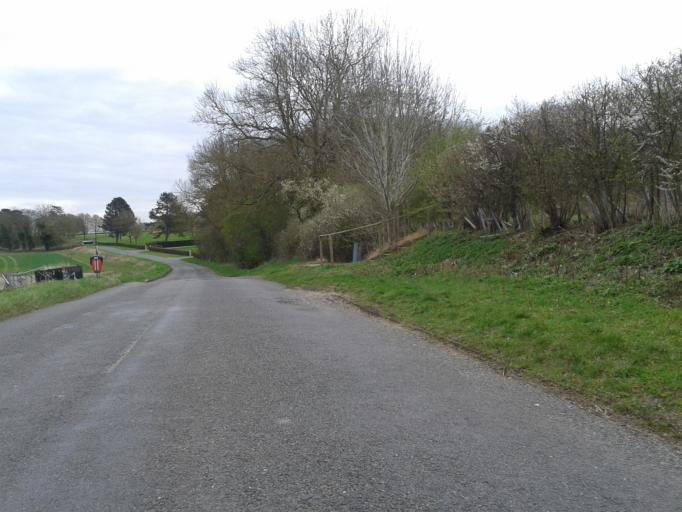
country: GB
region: England
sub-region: Cambridgeshire
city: Girton
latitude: 52.2199
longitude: 0.0516
